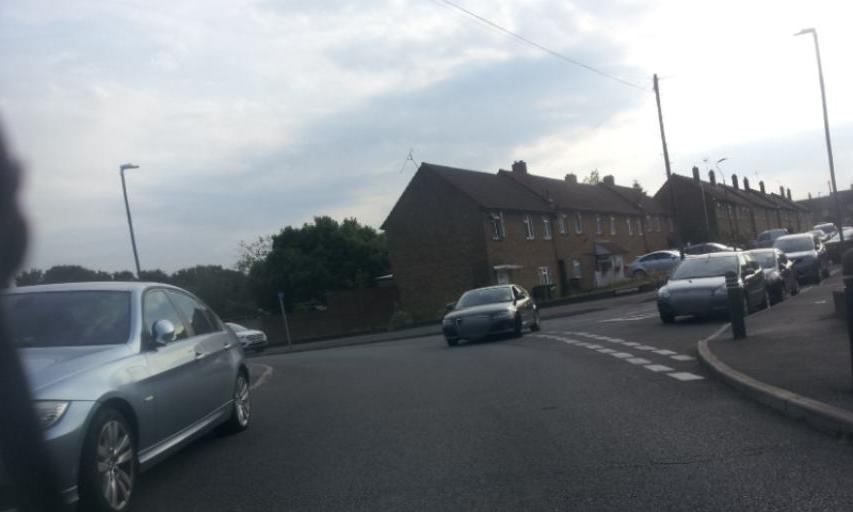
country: GB
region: England
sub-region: Greater London
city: Erith
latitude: 51.4656
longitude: 0.1772
